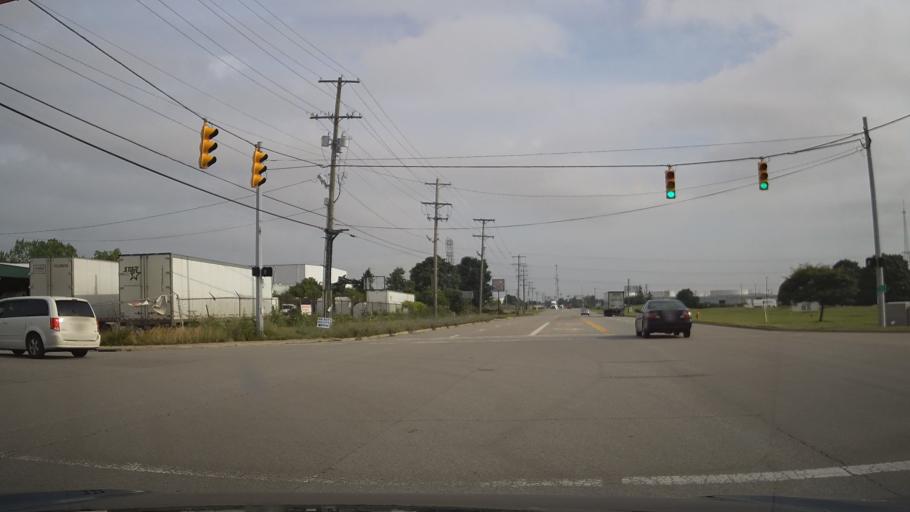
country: US
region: Ohio
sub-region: Franklin County
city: Lincoln Village
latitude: 39.9604
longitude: -83.1110
